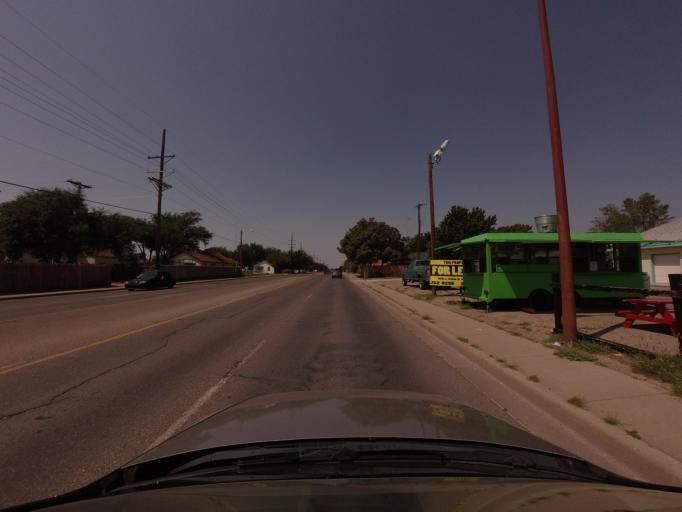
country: US
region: New Mexico
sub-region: Curry County
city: Clovis
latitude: 34.4194
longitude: -103.1981
